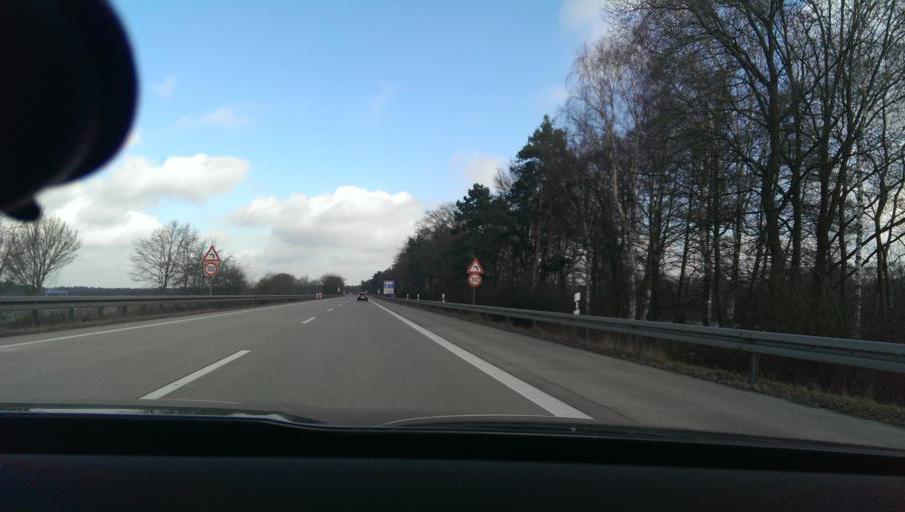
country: DE
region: Lower Saxony
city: Elze
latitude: 52.5373
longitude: 9.7954
